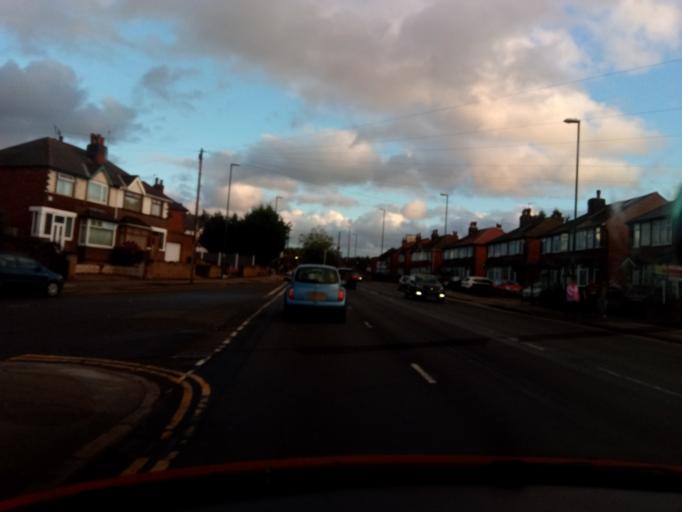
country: GB
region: England
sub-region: Nottingham
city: Nottingham
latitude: 52.9657
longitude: -1.1816
